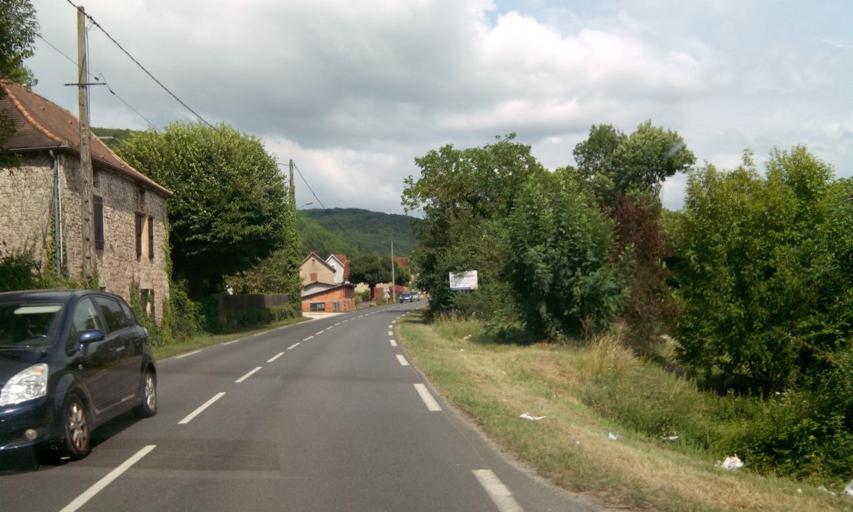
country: FR
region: Aquitaine
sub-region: Departement de la Dordogne
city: Eyvigues-et-Eybenes
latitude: 44.8876
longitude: 1.3851
